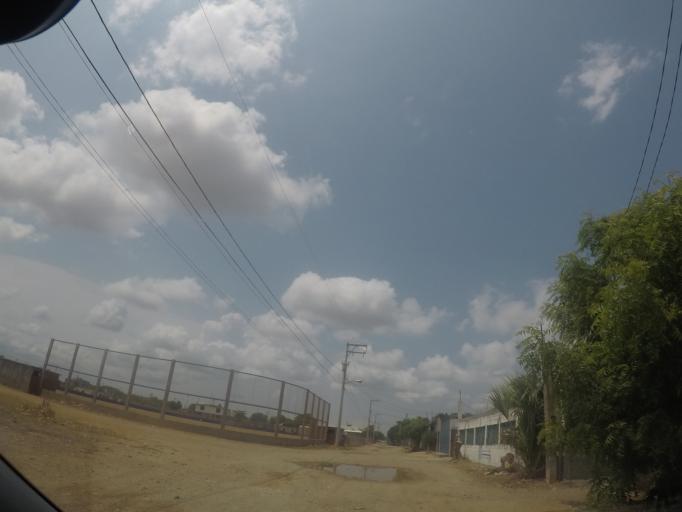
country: MX
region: Oaxaca
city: El Espinal
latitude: 16.5581
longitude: -94.9467
